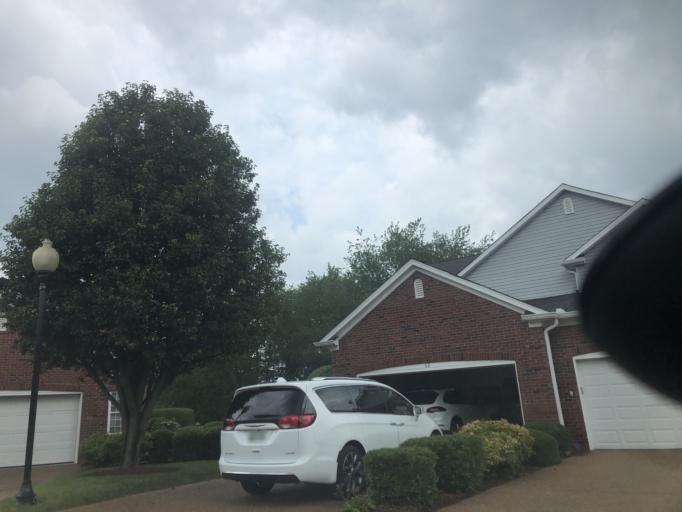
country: US
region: Tennessee
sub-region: Wilson County
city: Green Hill
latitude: 36.2450
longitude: -86.5850
